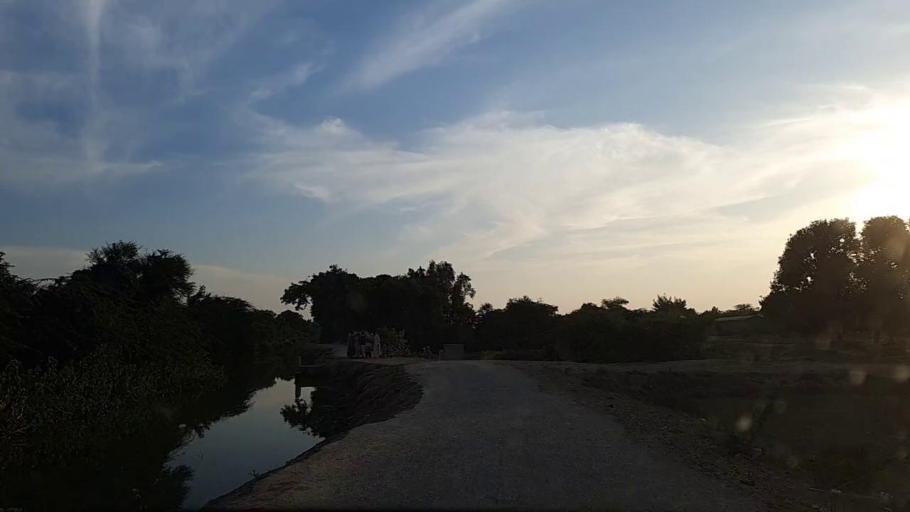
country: PK
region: Sindh
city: Mirpur Batoro
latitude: 24.6387
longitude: 68.1373
